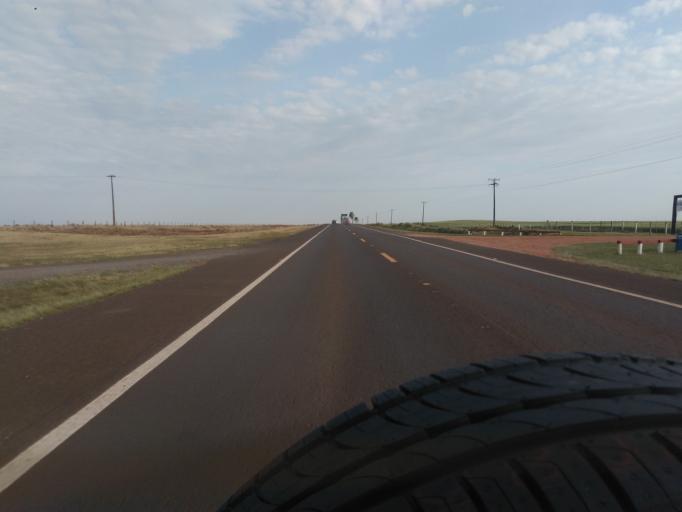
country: BR
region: Mato Grosso do Sul
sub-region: Ponta Pora
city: Ponta Pora
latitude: -22.6181
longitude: -55.5816
